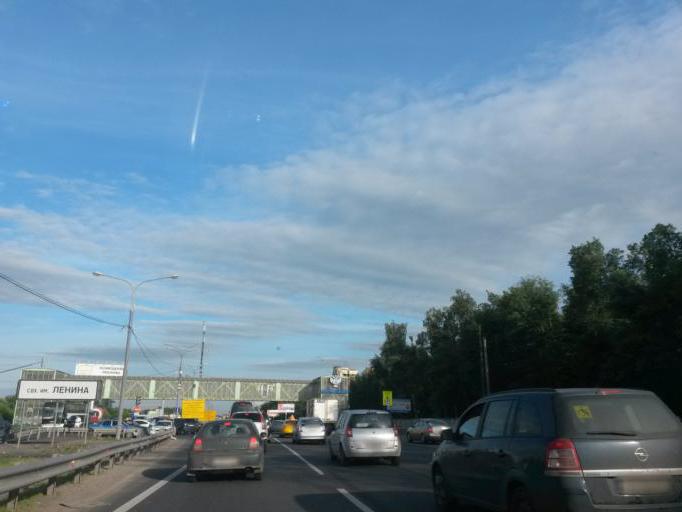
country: RU
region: Moskovskaya
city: Razvilka
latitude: 55.5890
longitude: 37.7324
